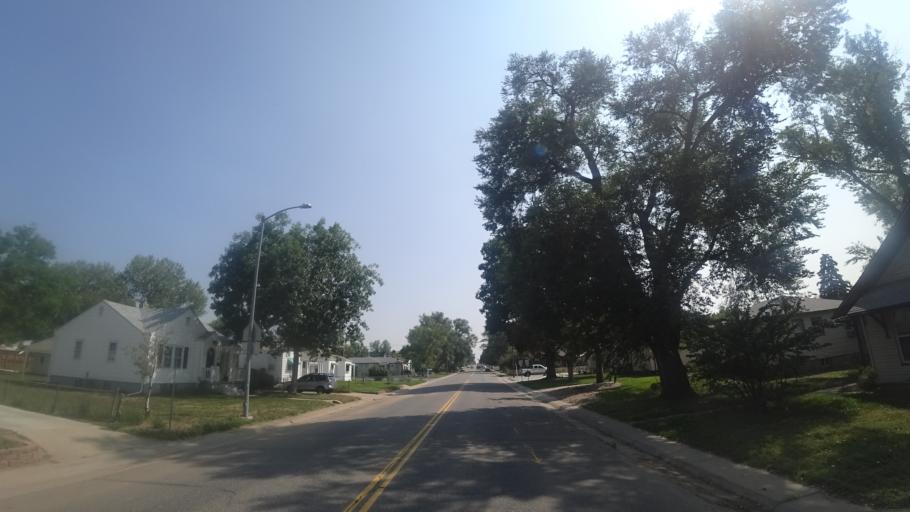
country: US
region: Colorado
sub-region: Arapahoe County
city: Englewood
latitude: 39.6447
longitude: -104.9831
